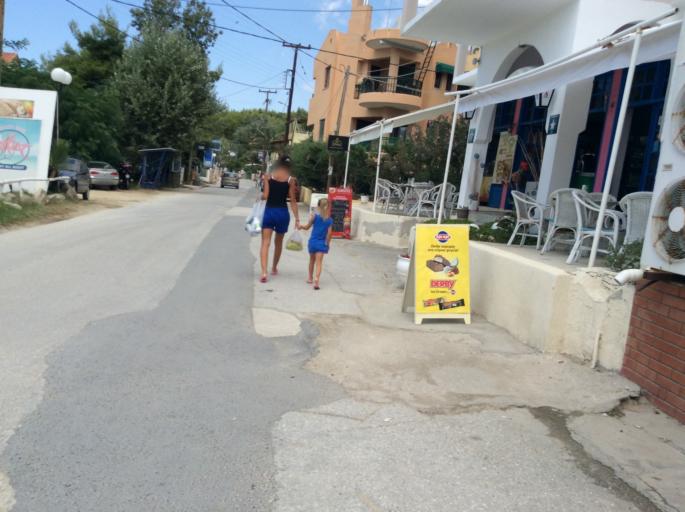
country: GR
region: Central Macedonia
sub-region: Nomos Chalkidikis
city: Sykia
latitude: 39.9887
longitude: 23.8991
